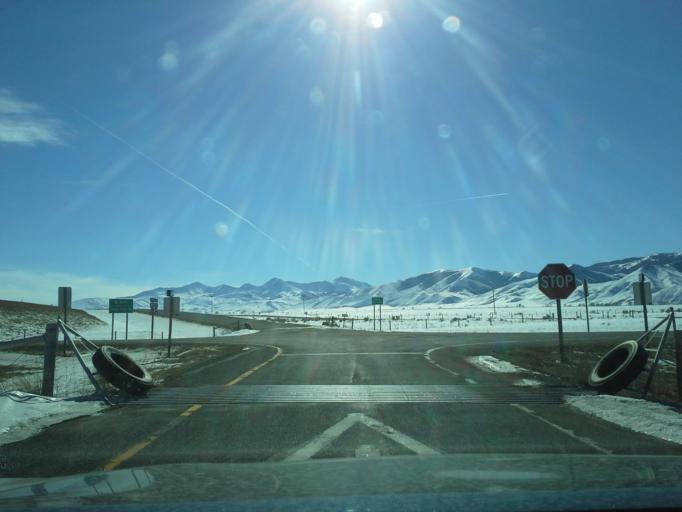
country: US
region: Montana
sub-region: Beaverhead County
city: Dillon
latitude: 44.7255
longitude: -112.7050
